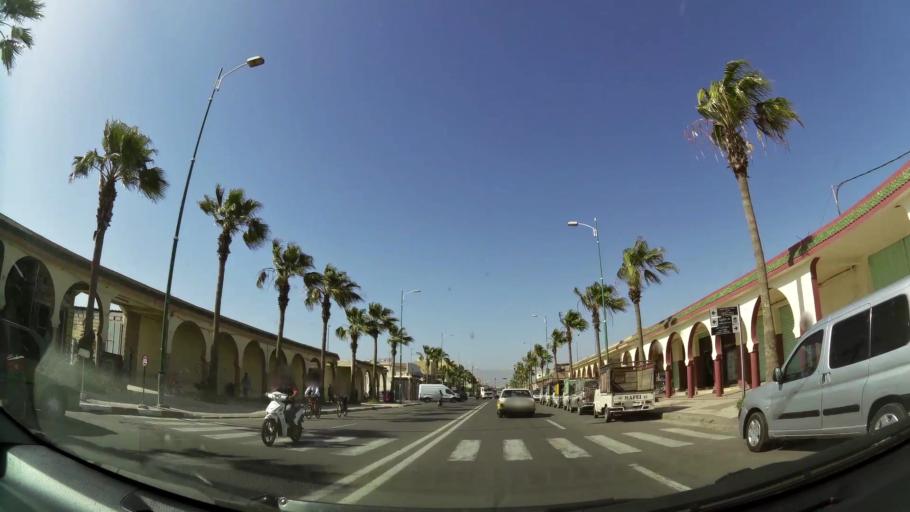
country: MA
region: Souss-Massa-Draa
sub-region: Inezgane-Ait Mellou
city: Inezgane
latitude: 30.3641
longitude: -9.5334
